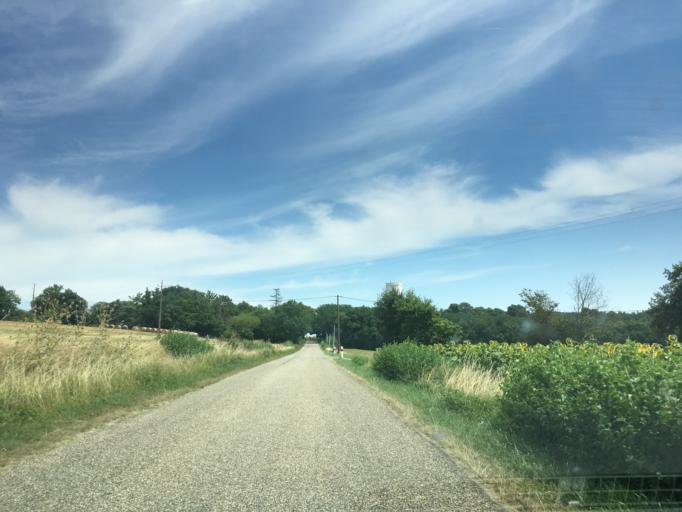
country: FR
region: Midi-Pyrenees
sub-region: Departement du Gers
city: Fleurance
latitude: 43.8186
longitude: 0.5994
